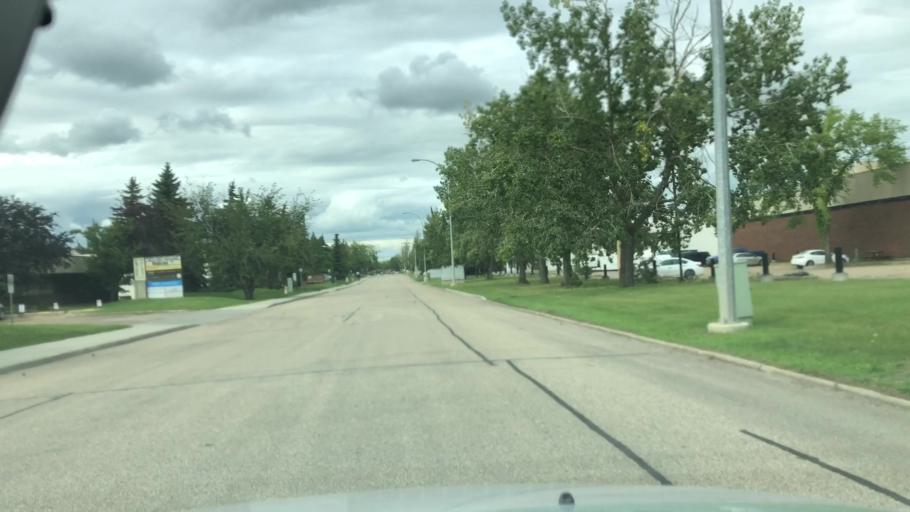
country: CA
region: Alberta
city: Edmonton
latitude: 53.5308
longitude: -113.4149
